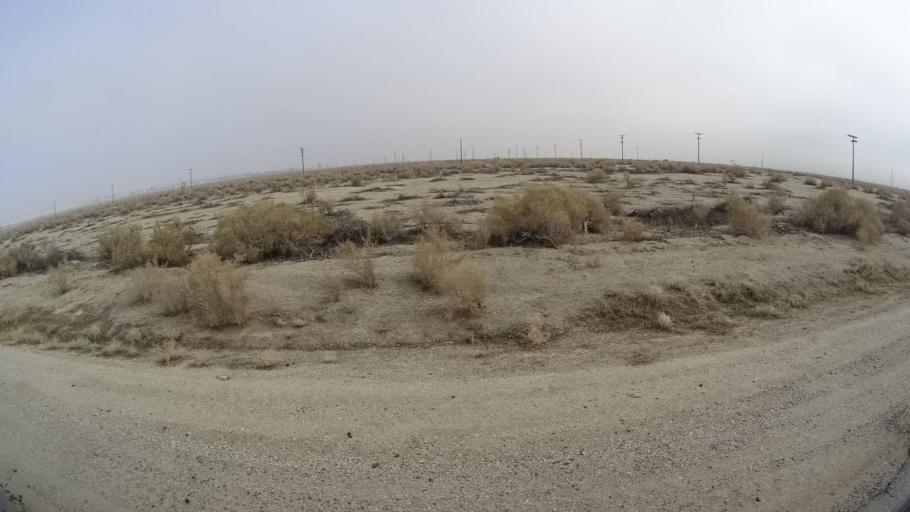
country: US
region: California
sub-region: Kern County
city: Ford City
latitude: 35.1971
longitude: -119.4290
